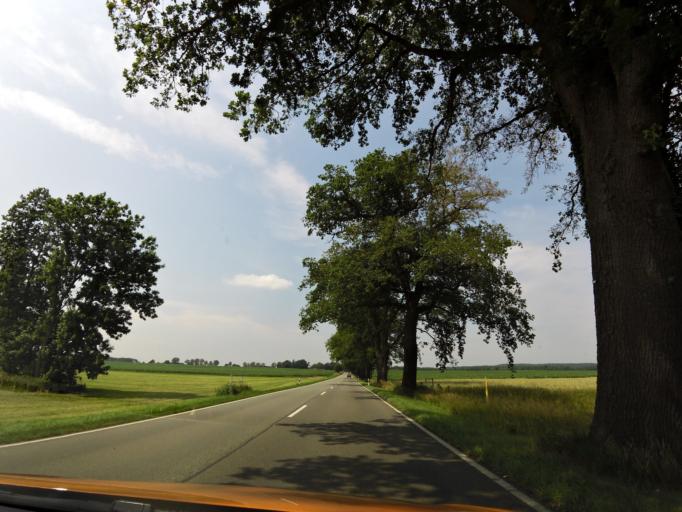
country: DE
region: Brandenburg
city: Gumtow
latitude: 53.0211
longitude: 12.3134
